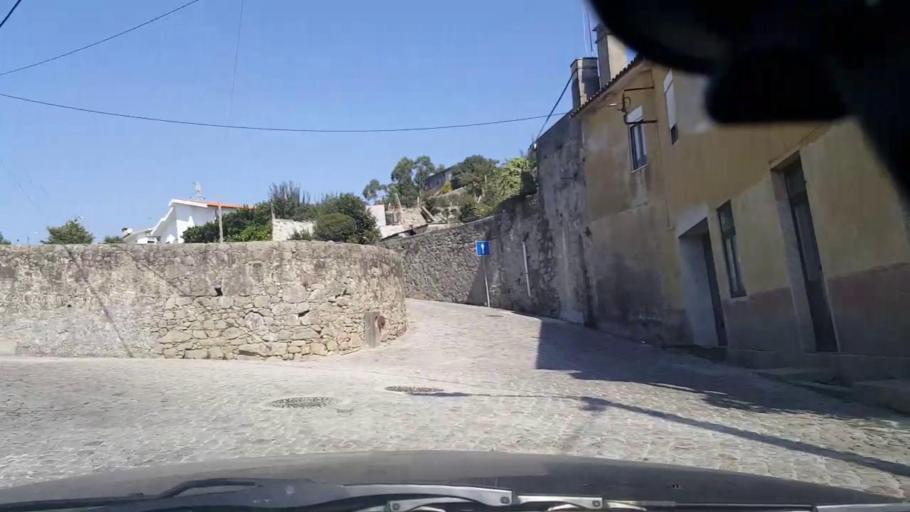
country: PT
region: Porto
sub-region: Vila do Conde
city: Arvore
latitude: 41.3753
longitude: -8.7024
